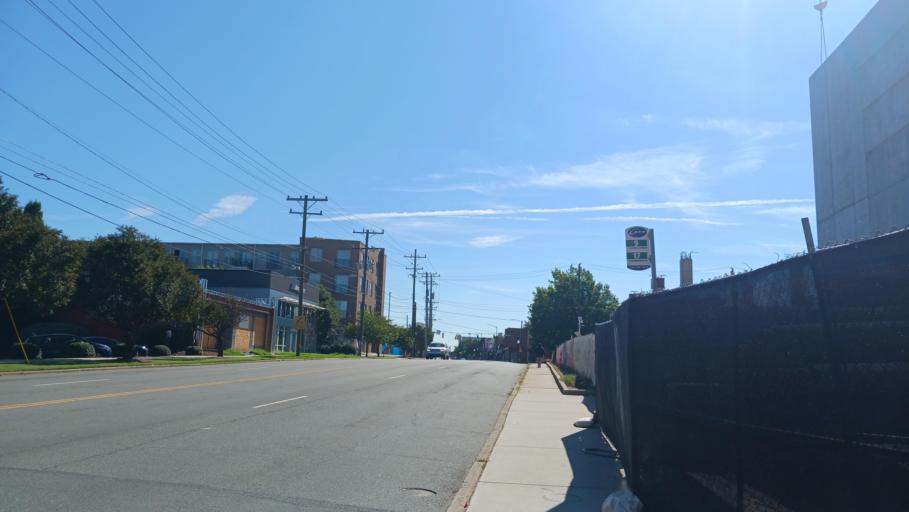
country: US
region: North Carolina
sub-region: Mecklenburg County
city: Charlotte
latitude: 35.2206
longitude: -80.8152
